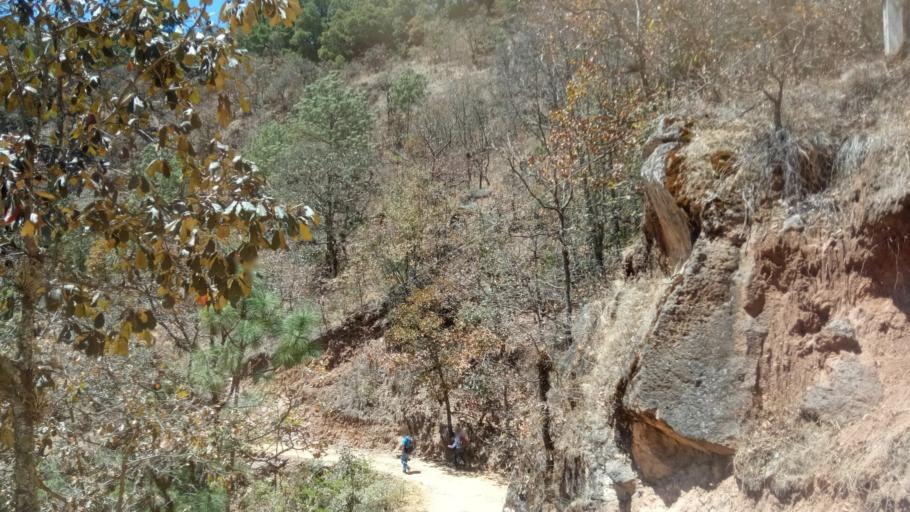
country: GT
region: San Marcos
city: Tejutla
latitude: 15.1335
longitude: -91.7927
